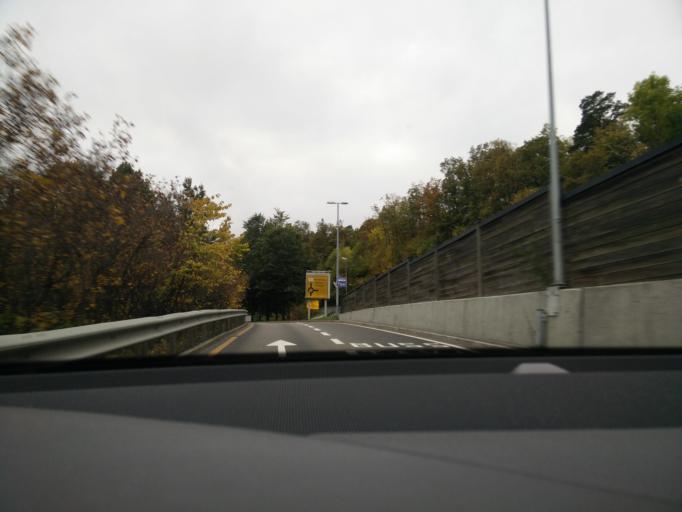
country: NO
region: Akershus
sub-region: Baerum
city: Lysaker
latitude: 59.9264
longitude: 10.6504
